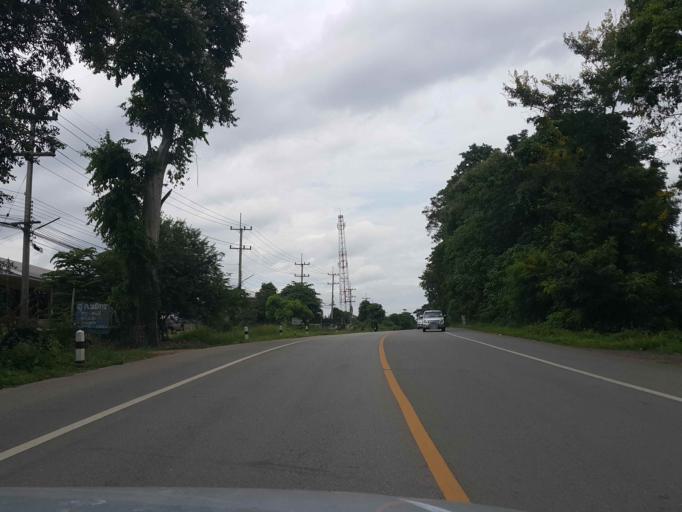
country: TH
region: Lamphun
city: Li
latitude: 17.7896
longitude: 98.9529
